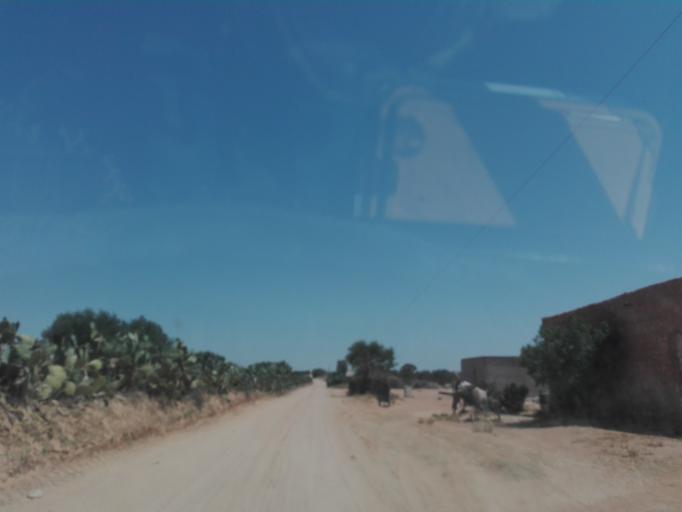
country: TN
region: Safaqis
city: Bi'r `Ali Bin Khalifah
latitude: 34.6628
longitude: 10.2397
